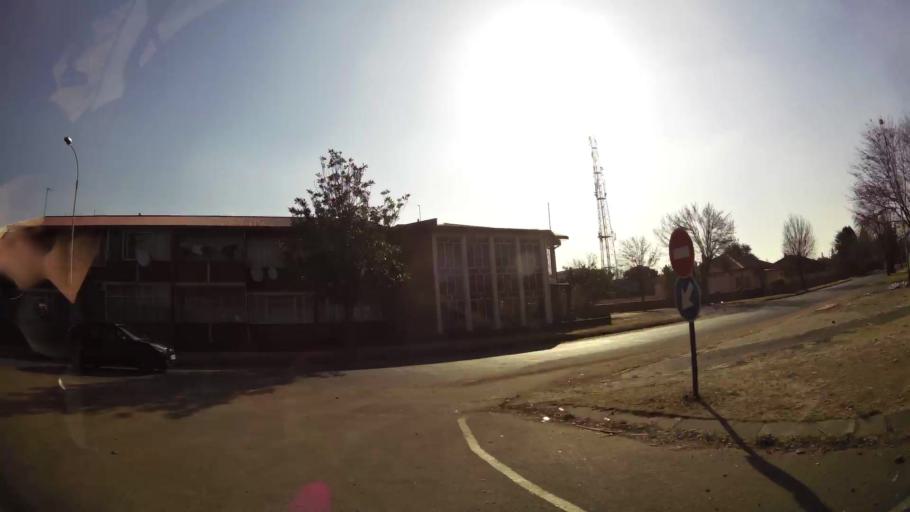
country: ZA
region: Gauteng
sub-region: West Rand District Municipality
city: Randfontein
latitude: -26.1785
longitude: 27.7062
